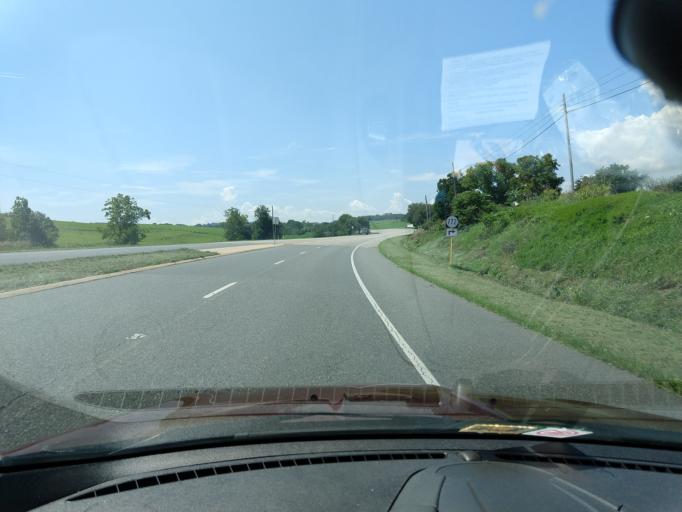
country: US
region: Virginia
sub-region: City of Harrisonburg
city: Harrisonburg
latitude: 38.5119
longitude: -78.8691
